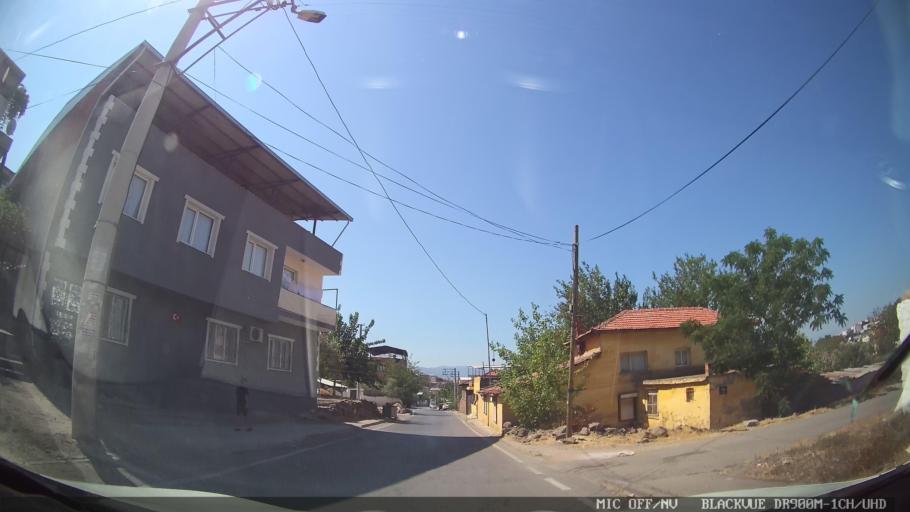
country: TR
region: Izmir
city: Karsiyaka
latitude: 38.5008
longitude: 27.0697
